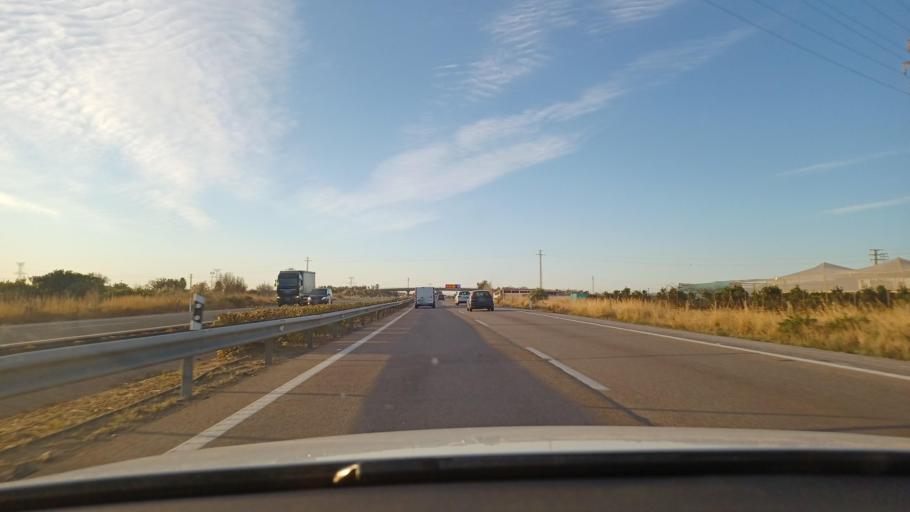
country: ES
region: Valencia
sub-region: Provincia de Castello
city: Vila-real
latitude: 39.9557
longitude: -0.1292
